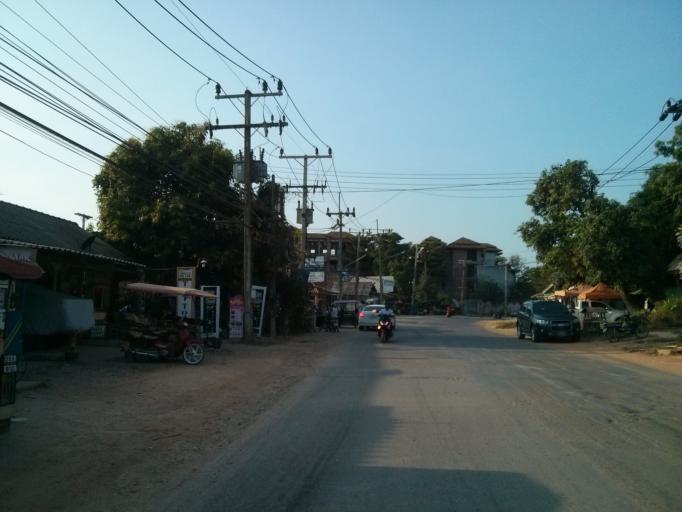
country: TH
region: Krabi
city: Saladan
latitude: 7.5817
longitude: 99.0336
